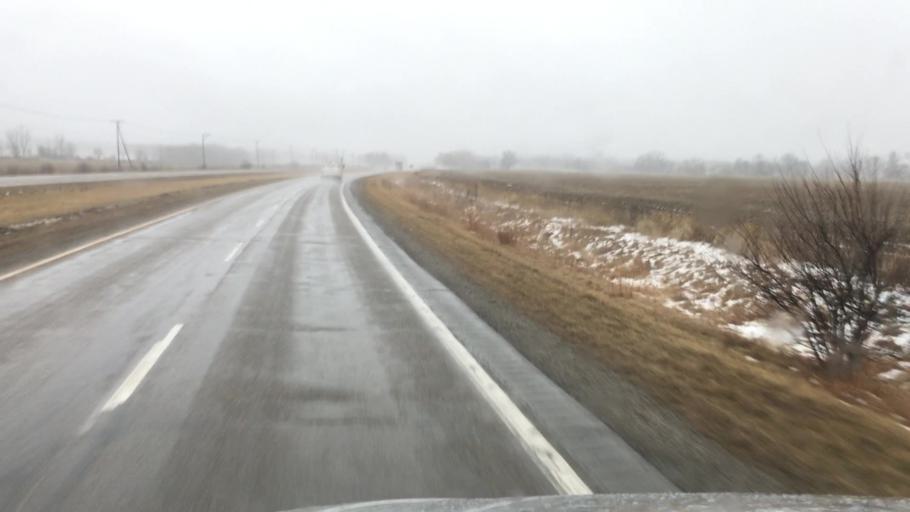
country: US
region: Indiana
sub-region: Newton County
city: Roselawn
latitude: 41.1206
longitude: -87.4492
